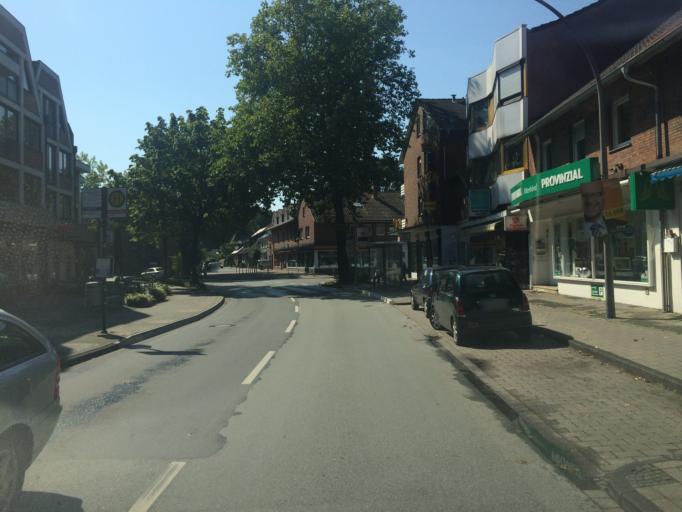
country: DE
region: North Rhine-Westphalia
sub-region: Regierungsbezirk Munster
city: Muenster
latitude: 51.9876
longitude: 7.6988
